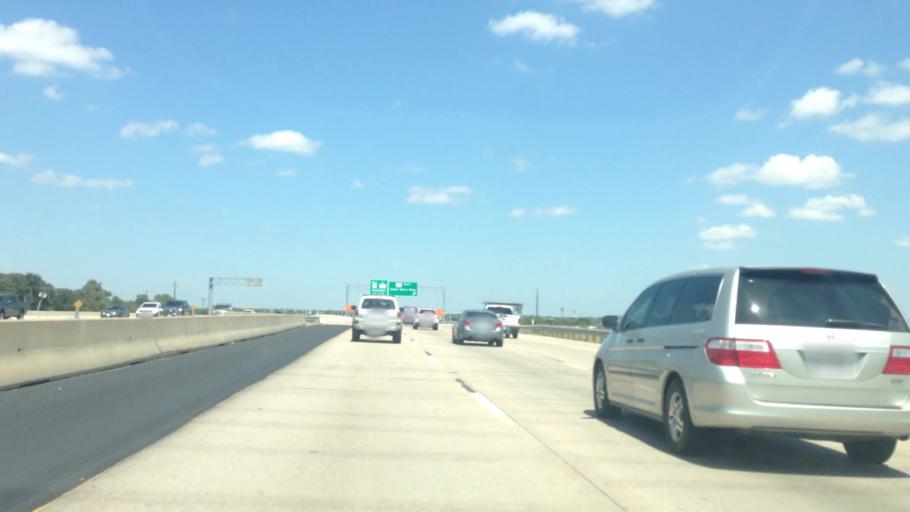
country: US
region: Texas
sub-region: Tarrant County
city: Grapevine
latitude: 32.8921
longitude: -97.0991
